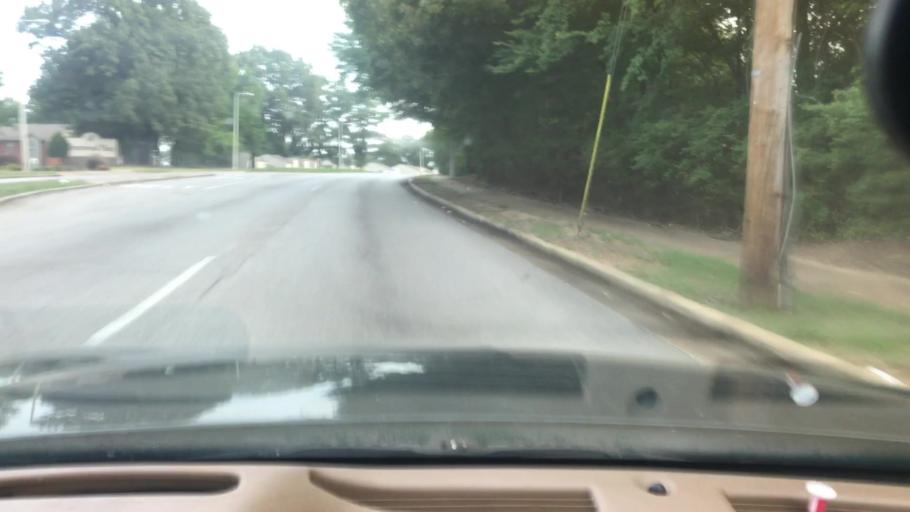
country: US
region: Tennessee
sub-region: Shelby County
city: Bartlett
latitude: 35.1753
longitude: -89.8707
